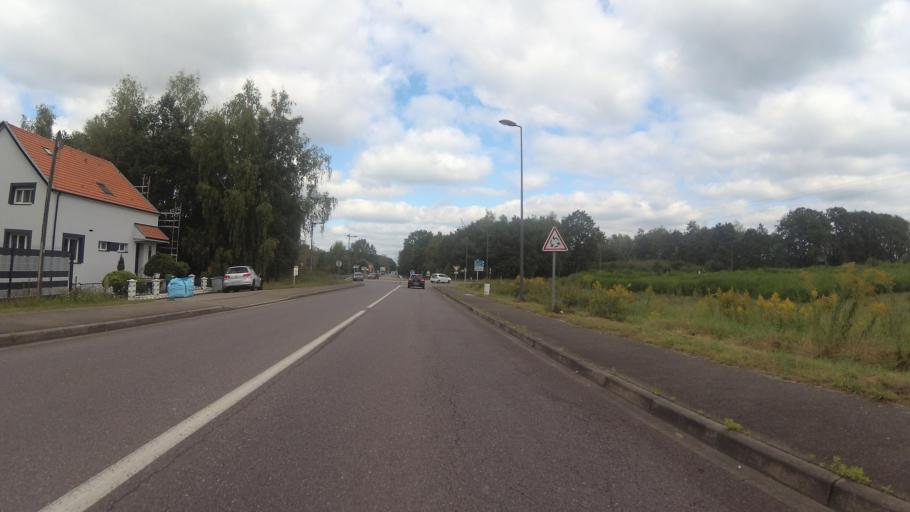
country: DE
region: Saarland
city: Uberherrn
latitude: 49.2140
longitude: 6.7149
